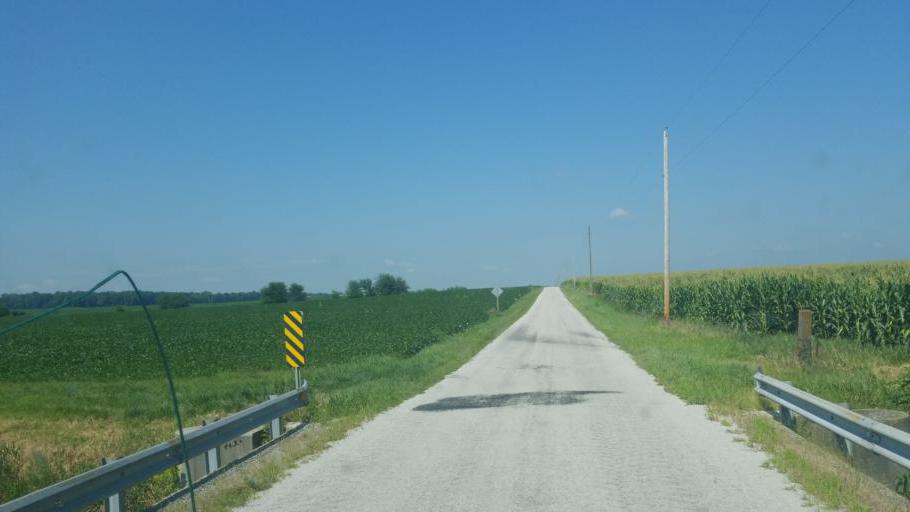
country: US
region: Ohio
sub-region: Hardin County
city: Kenton
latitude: 40.6747
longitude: -83.6140
